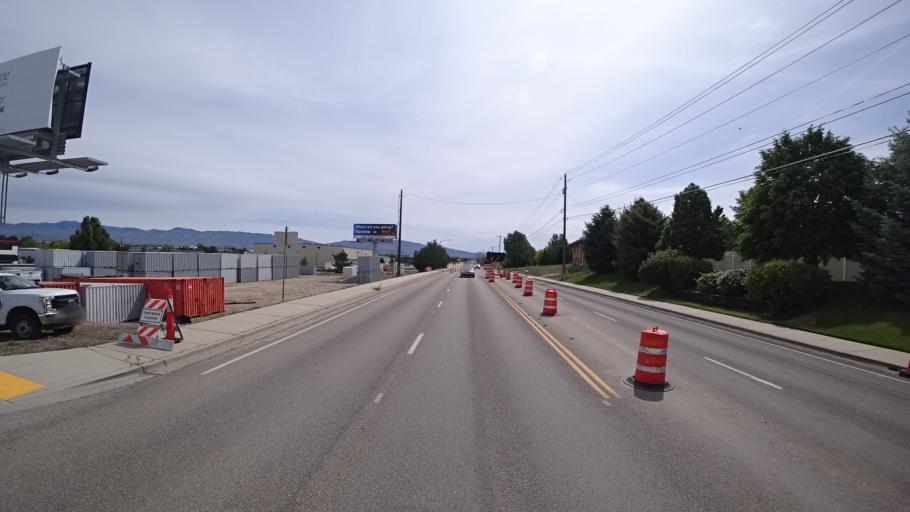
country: US
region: Idaho
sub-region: Ada County
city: Garden City
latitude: 43.5756
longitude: -116.2800
